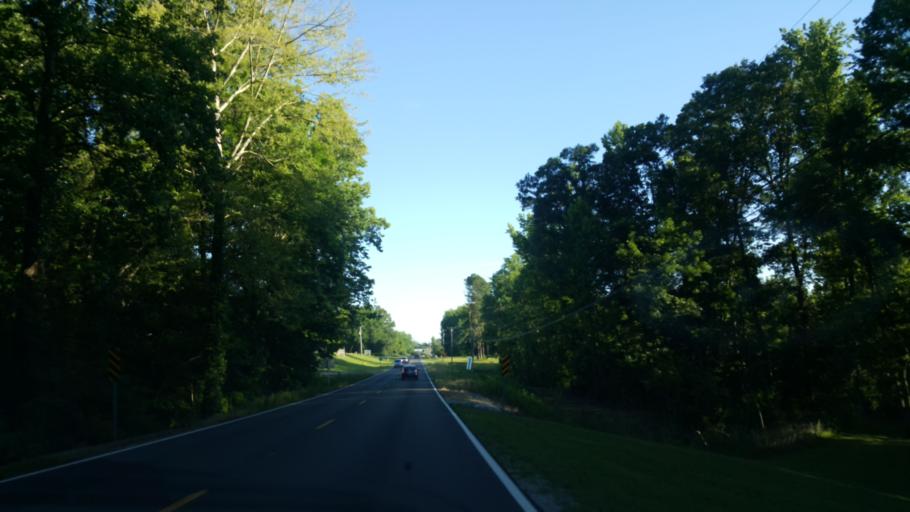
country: US
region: Tennessee
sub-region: Henderson County
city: Lexington
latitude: 35.6141
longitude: -88.4005
